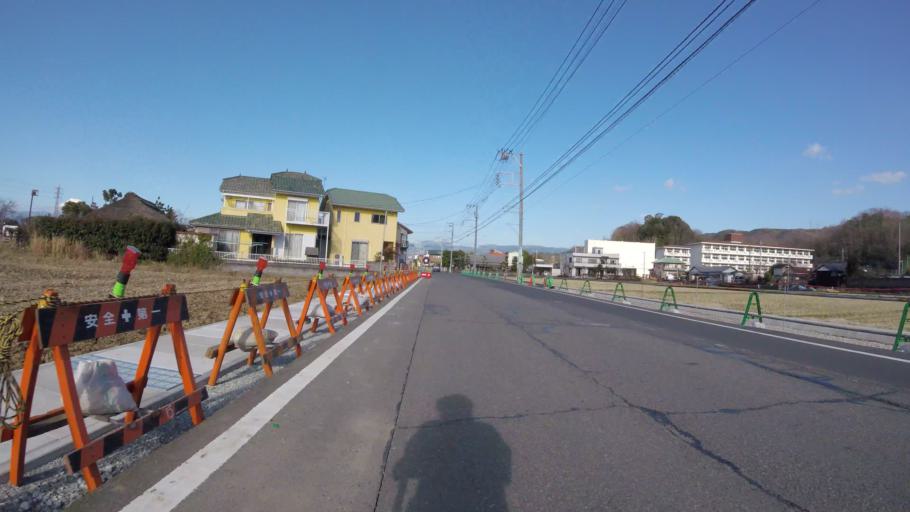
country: JP
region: Shizuoka
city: Mishima
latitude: 35.0512
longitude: 138.9524
